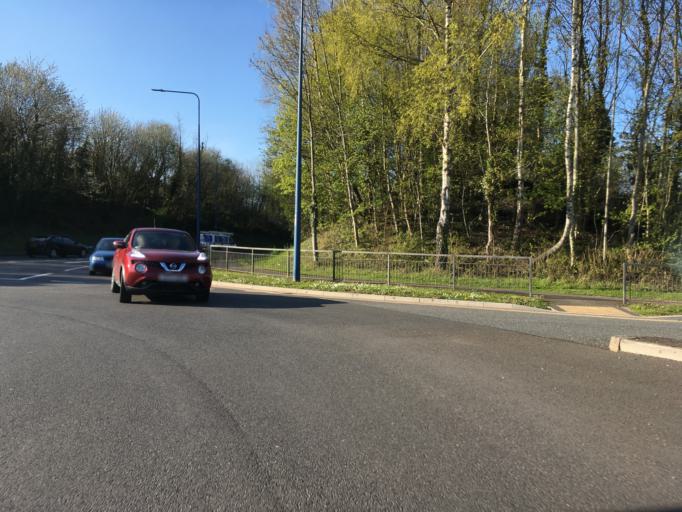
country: GB
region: Wales
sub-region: Torfaen County Borough
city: Cwmbran
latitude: 51.6675
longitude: -3.0219
